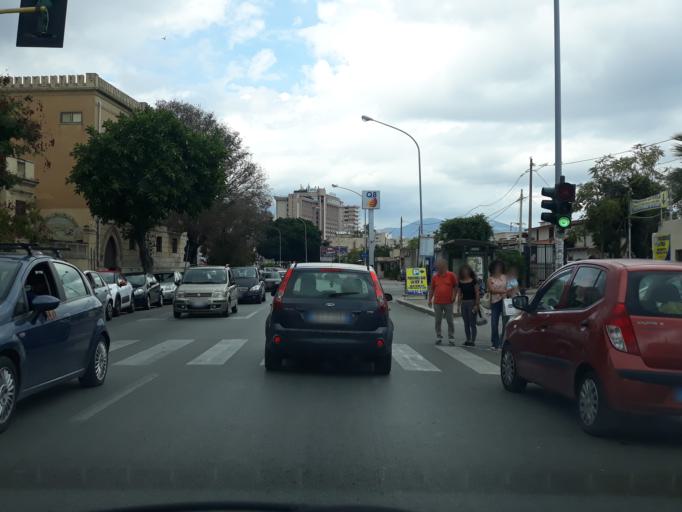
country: IT
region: Sicily
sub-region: Palermo
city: Ciaculli
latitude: 38.1063
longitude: 13.3860
